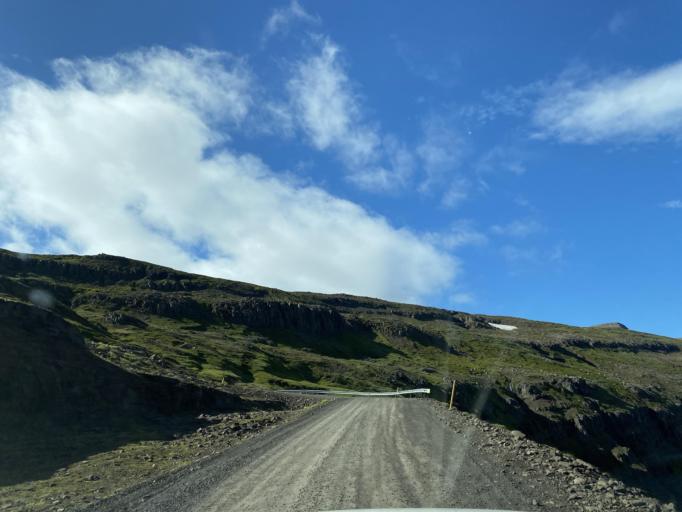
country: IS
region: East
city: Eskifjoerdur
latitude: 65.1799
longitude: -14.0863
